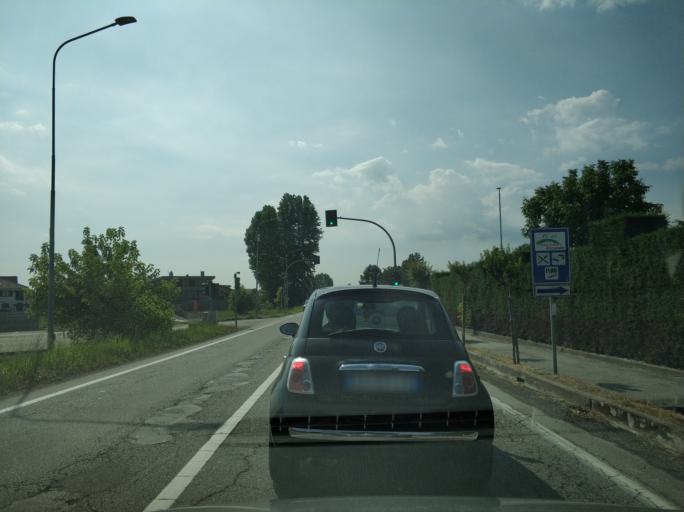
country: IT
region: Piedmont
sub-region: Provincia di Torino
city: Marocchi
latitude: 44.9411
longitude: 7.8186
